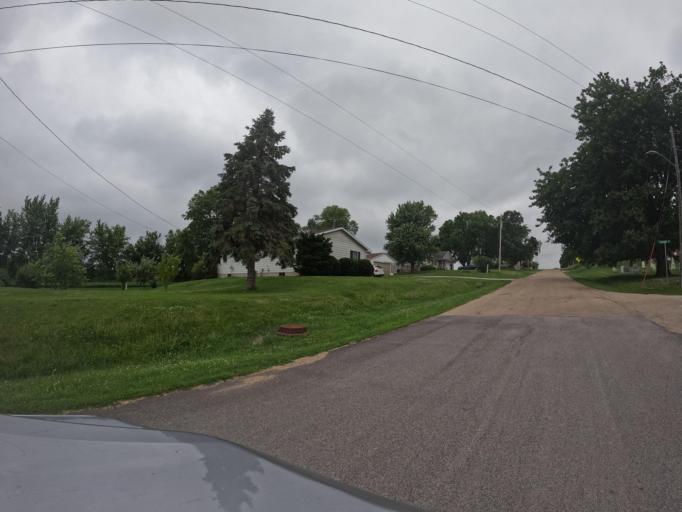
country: US
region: Iowa
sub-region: Clinton County
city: De Witt
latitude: 41.9128
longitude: -90.6013
